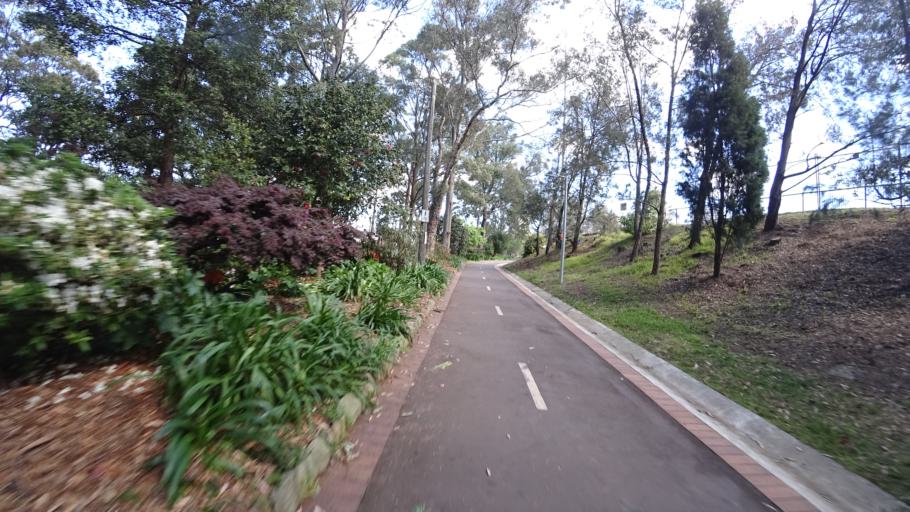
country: AU
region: New South Wales
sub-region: Willoughby
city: Chatswood
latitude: -33.7910
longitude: 151.1869
